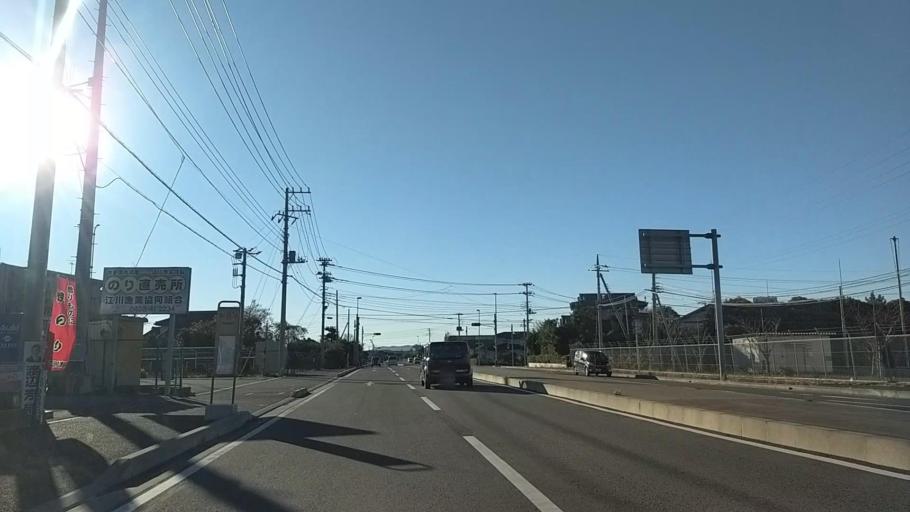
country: JP
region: Chiba
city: Kisarazu
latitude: 35.4041
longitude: 139.9191
